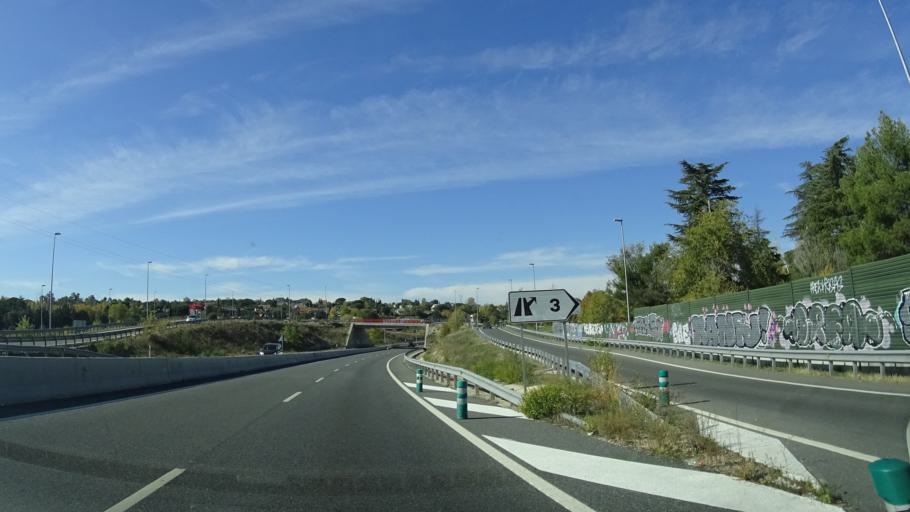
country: ES
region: Madrid
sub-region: Provincia de Madrid
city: Villanueva del Pardillo
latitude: 40.4849
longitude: -3.9383
